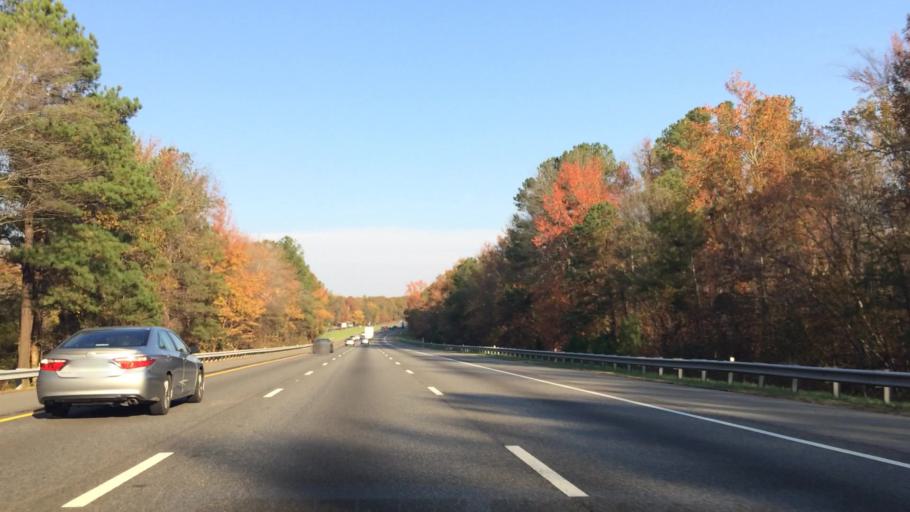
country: US
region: Virginia
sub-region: Caroline County
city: Bowling Green
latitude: 37.9648
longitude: -77.4880
